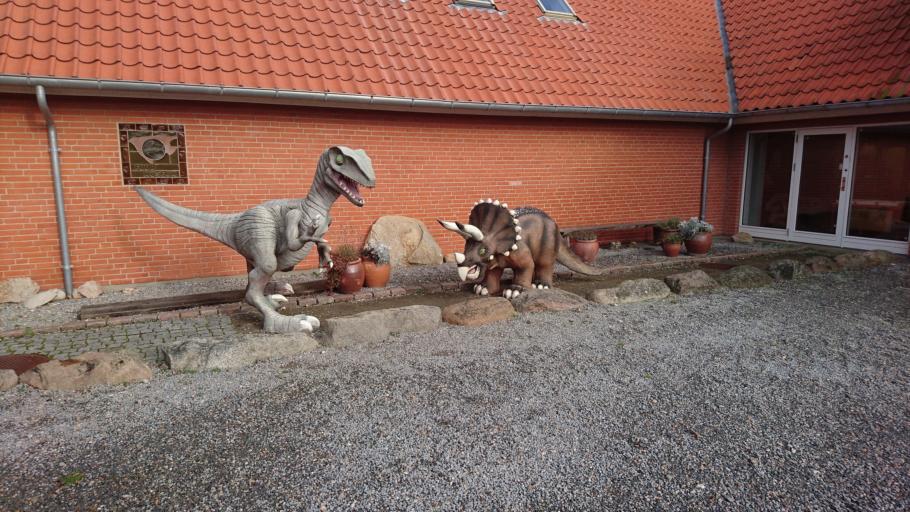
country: DK
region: North Denmark
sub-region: Morso Kommune
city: Nykobing Mors
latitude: 56.8167
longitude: 9.0217
